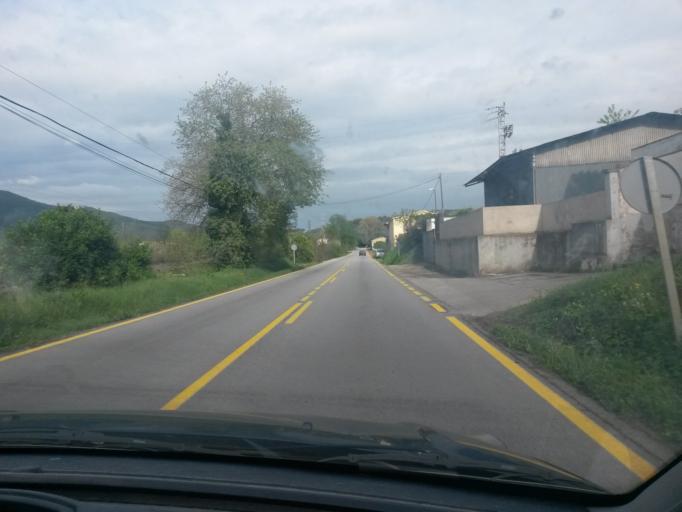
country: ES
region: Catalonia
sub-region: Provincia de Girona
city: Angles
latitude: 41.9719
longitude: 2.6791
